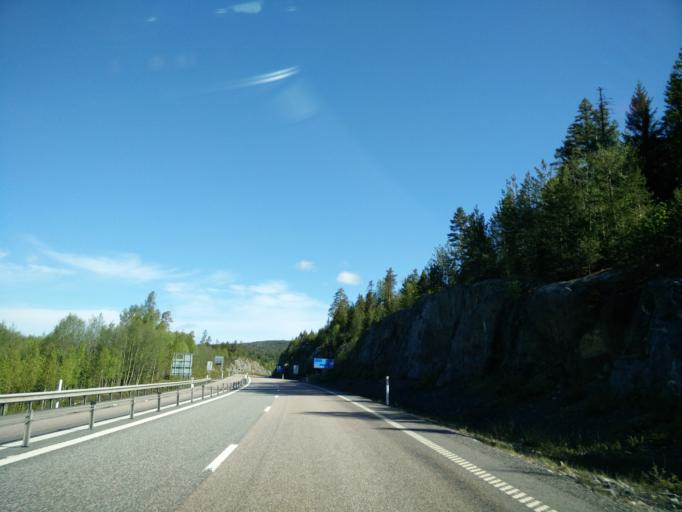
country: SE
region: Vaesternorrland
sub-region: Kramfors Kommun
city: Nordingra
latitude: 62.9425
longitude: 18.0944
